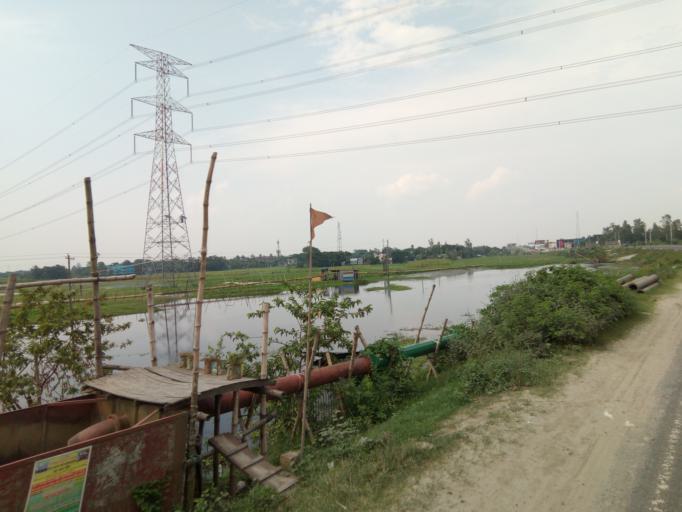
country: BD
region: Dhaka
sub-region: Dhaka
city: Dhaka
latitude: 23.6266
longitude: 90.3421
